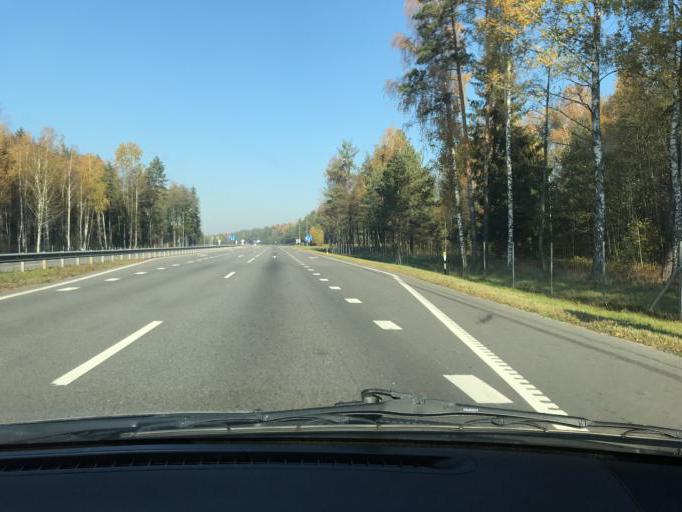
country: BY
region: Minsk
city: Slutsk
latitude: 53.2810
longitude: 27.5500
